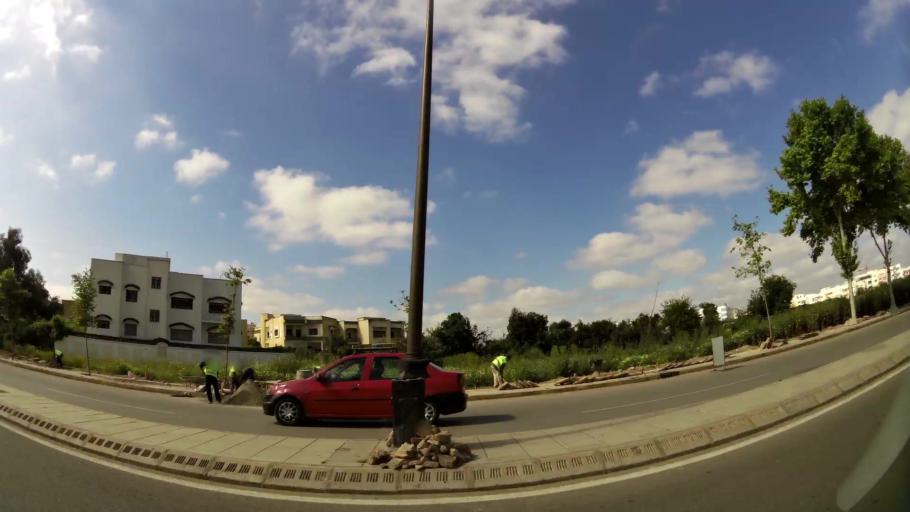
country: MA
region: Fes-Boulemane
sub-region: Fes
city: Fes
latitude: 34.0266
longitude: -5.0254
